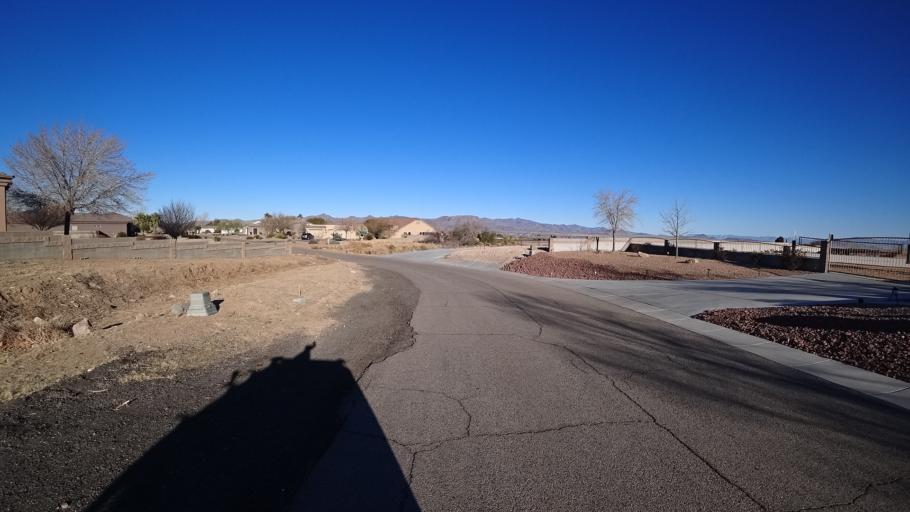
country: US
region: Arizona
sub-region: Mohave County
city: Kingman
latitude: 35.1947
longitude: -113.9950
